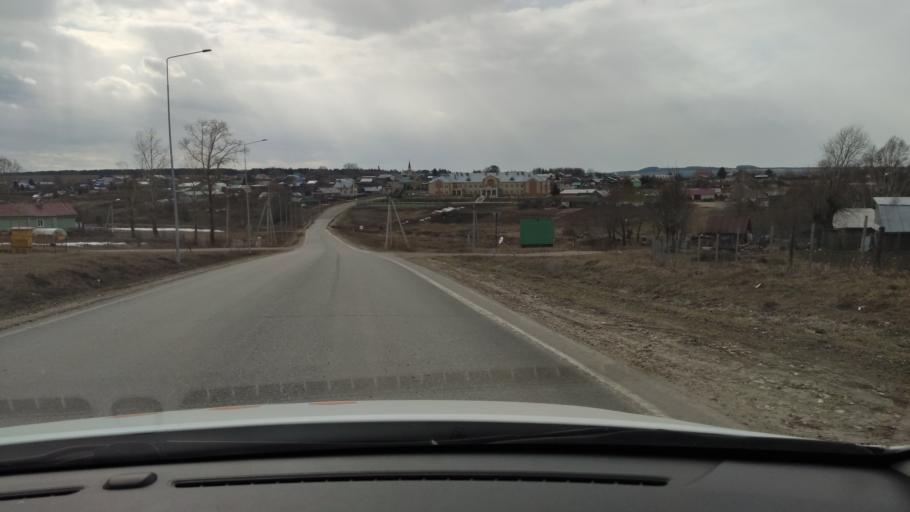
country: RU
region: Tatarstan
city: Vysokaya Gora
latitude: 56.2193
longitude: 49.2673
